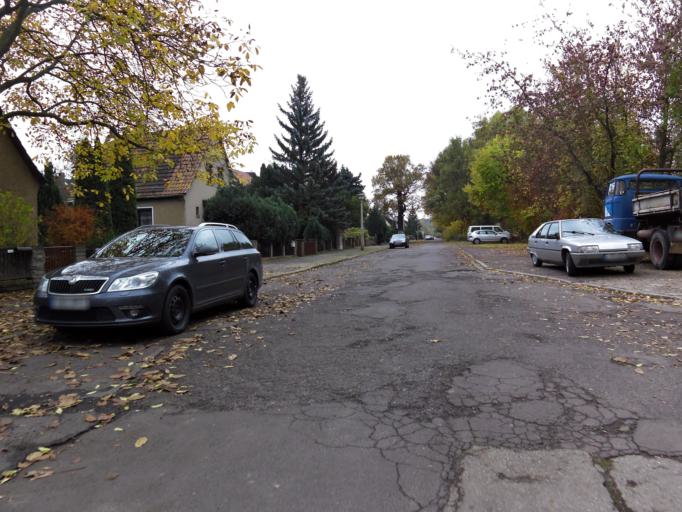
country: DE
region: Saxony
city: Leipzig
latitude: 51.3129
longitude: 12.3658
